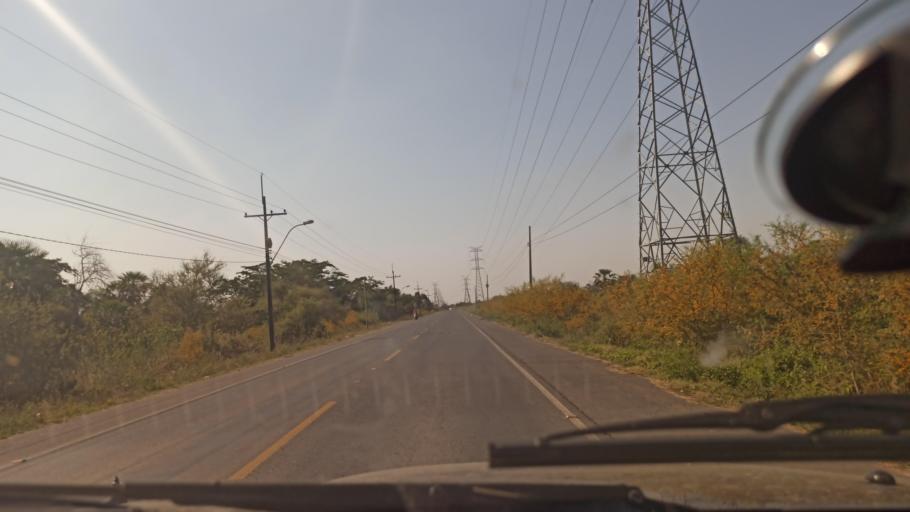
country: PY
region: Presidente Hayes
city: Nanawa
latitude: -25.2501
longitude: -57.6705
